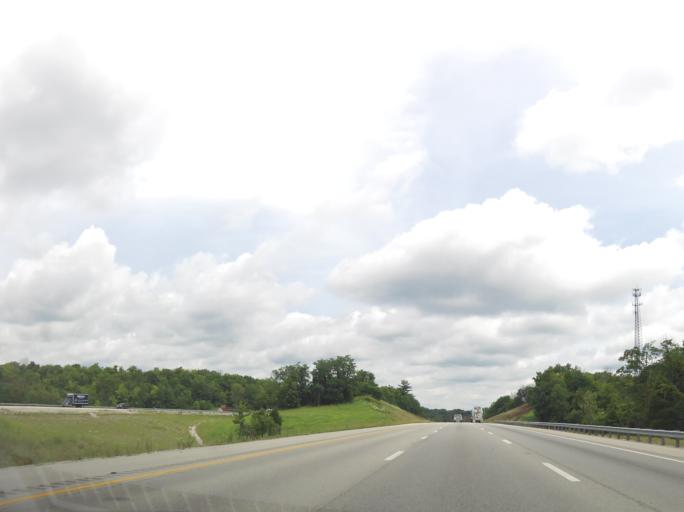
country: US
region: Kentucky
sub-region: Grant County
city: Williamstown
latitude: 38.4325
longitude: -84.5721
